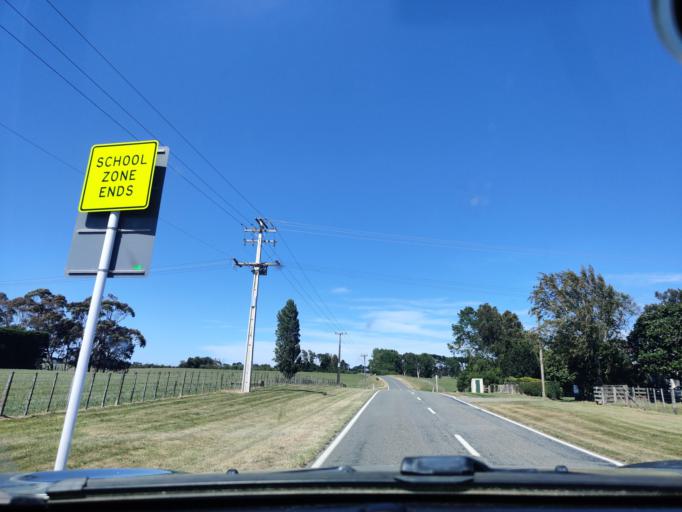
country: NZ
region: Wellington
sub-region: Upper Hutt City
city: Upper Hutt
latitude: -41.3546
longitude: 175.2040
